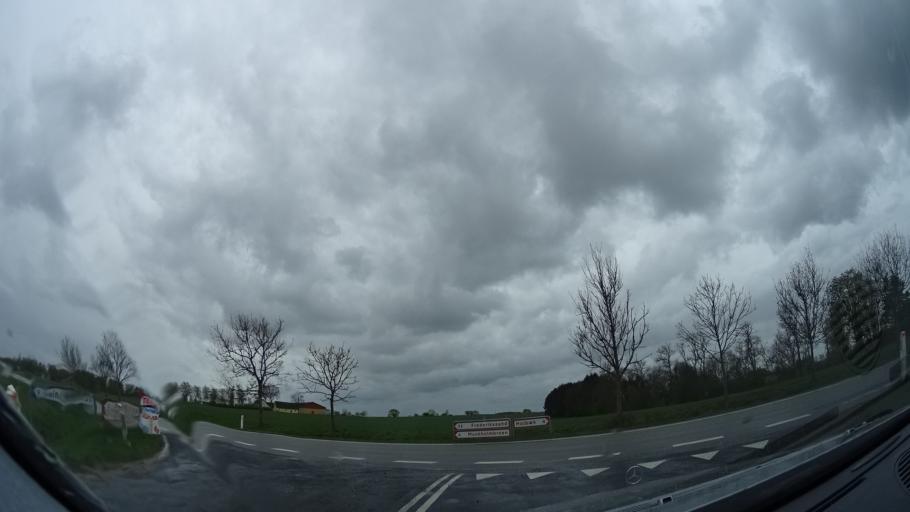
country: DK
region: Zealand
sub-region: Holbaek Kommune
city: Vipperod
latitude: 55.6999
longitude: 11.7798
